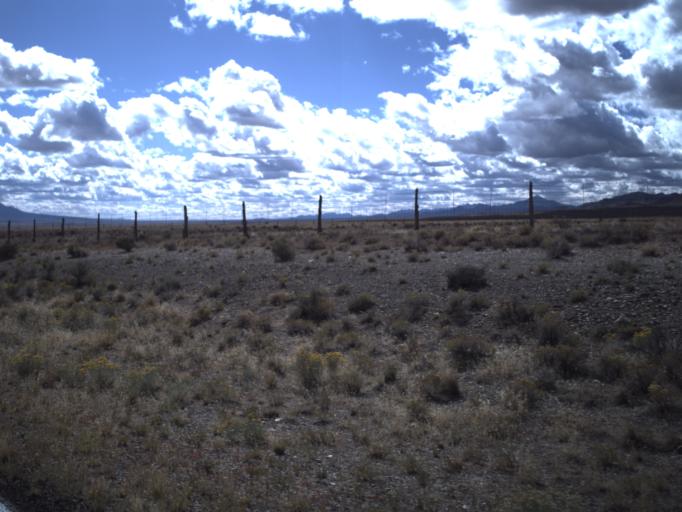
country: US
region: Utah
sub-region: Beaver County
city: Milford
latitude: 38.5903
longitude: -113.8192
